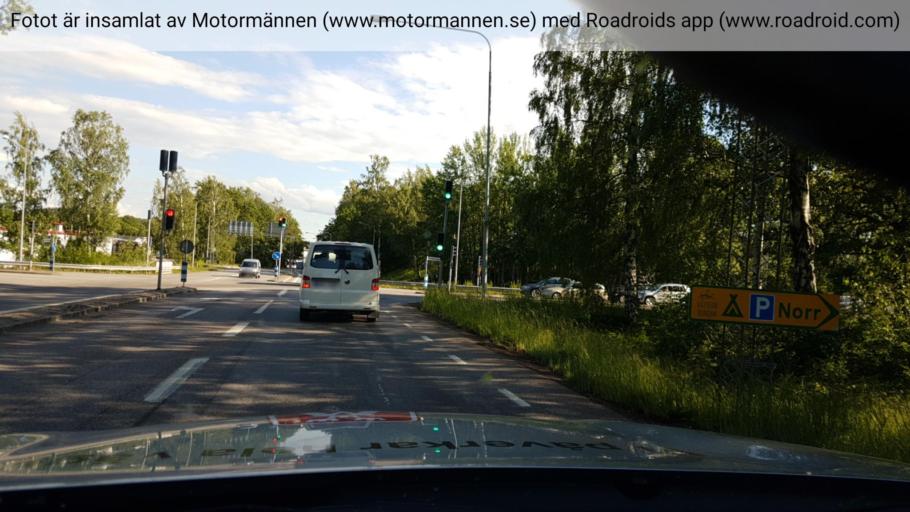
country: SE
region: OEstergoetland
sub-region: Motala Kommun
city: Motala
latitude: 58.5564
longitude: 15.0626
